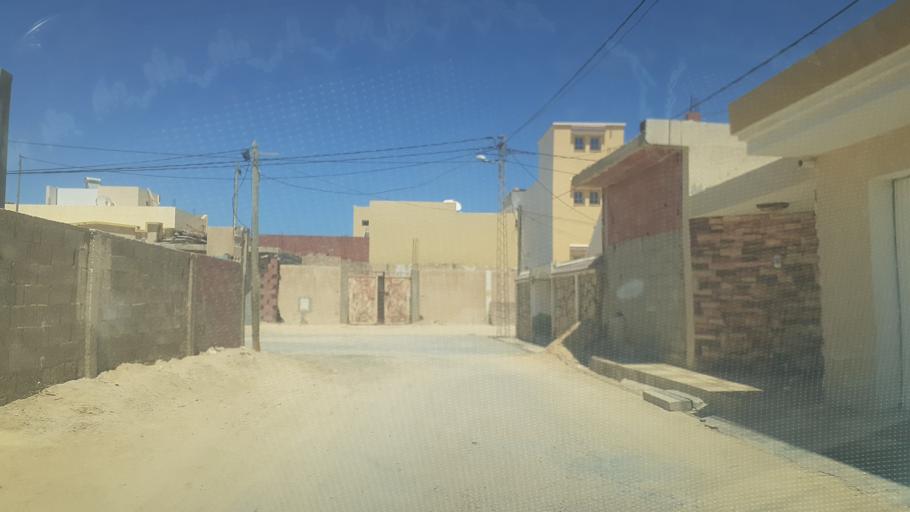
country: TN
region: Qabis
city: Gabes
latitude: 33.9329
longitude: 10.0606
